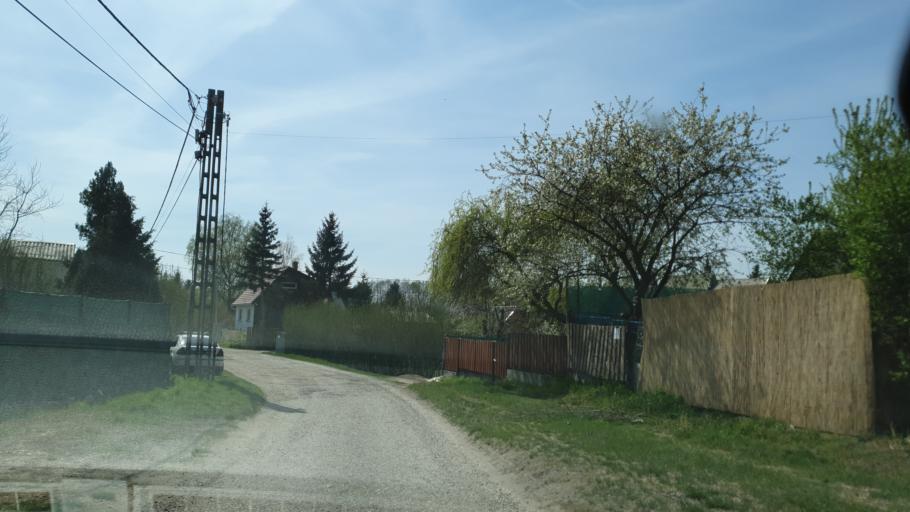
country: HU
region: Komarom-Esztergom
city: Oroszlany
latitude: 47.4966
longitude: 18.2864
